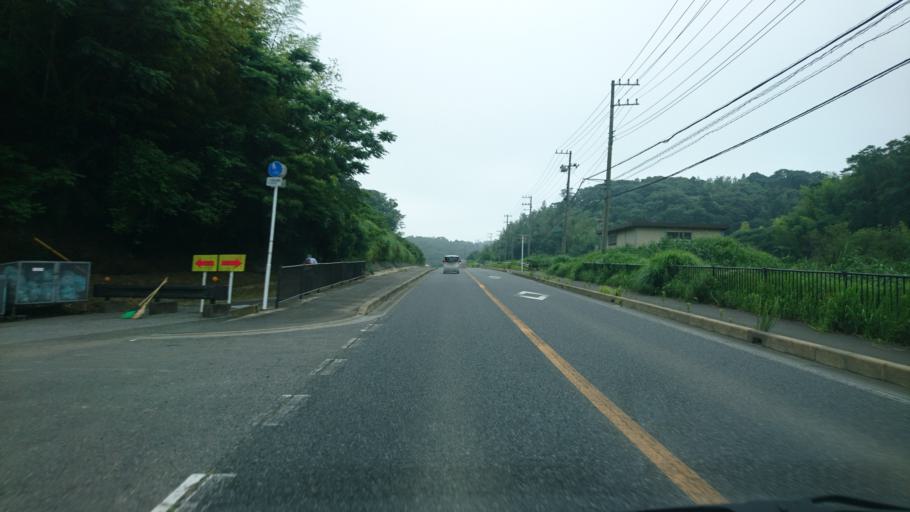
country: JP
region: Chiba
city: Kimitsu
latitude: 35.2564
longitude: 139.8841
